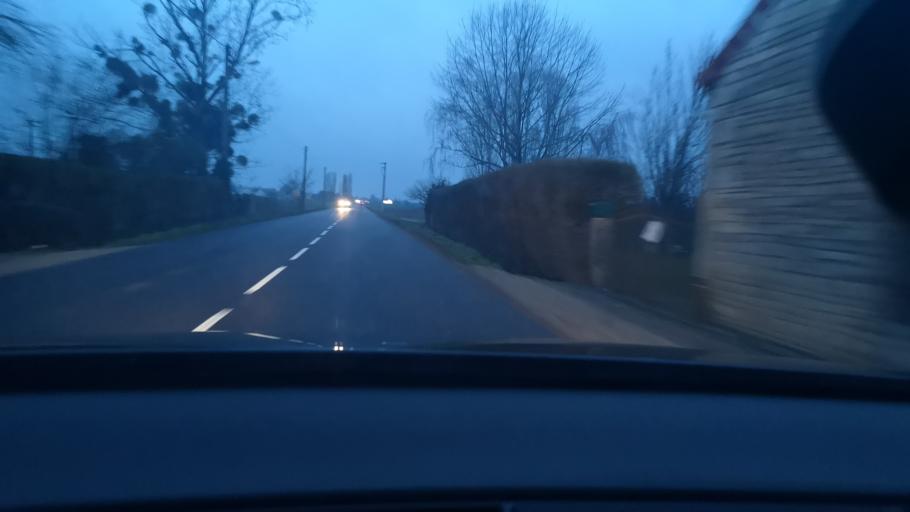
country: FR
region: Bourgogne
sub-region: Departement de Saone-et-Loire
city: Demigny
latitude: 46.9356
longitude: 4.8556
